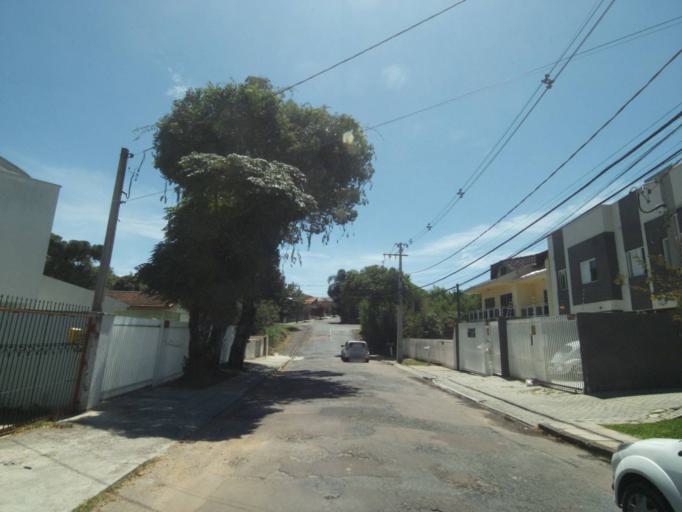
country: BR
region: Parana
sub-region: Curitiba
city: Curitiba
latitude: -25.4658
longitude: -49.2417
